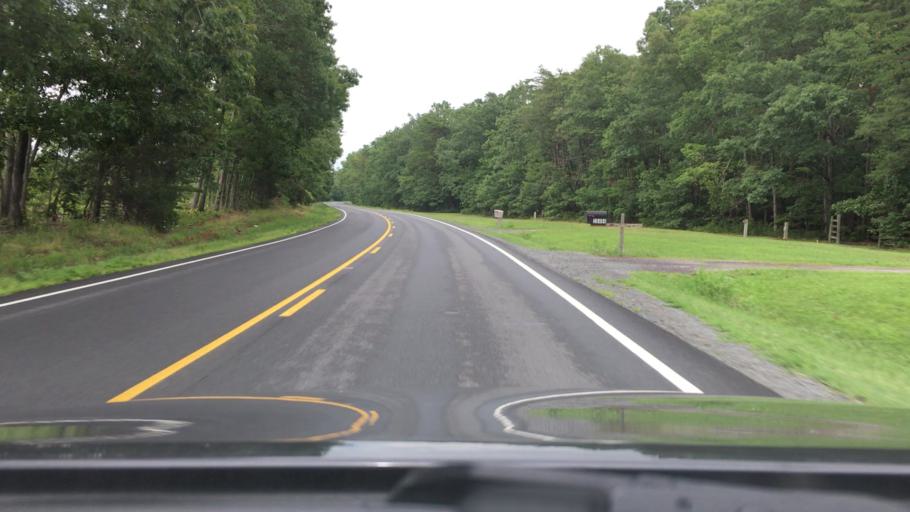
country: US
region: Virginia
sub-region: Culpeper County
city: Culpeper
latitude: 38.2812
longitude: -77.8755
